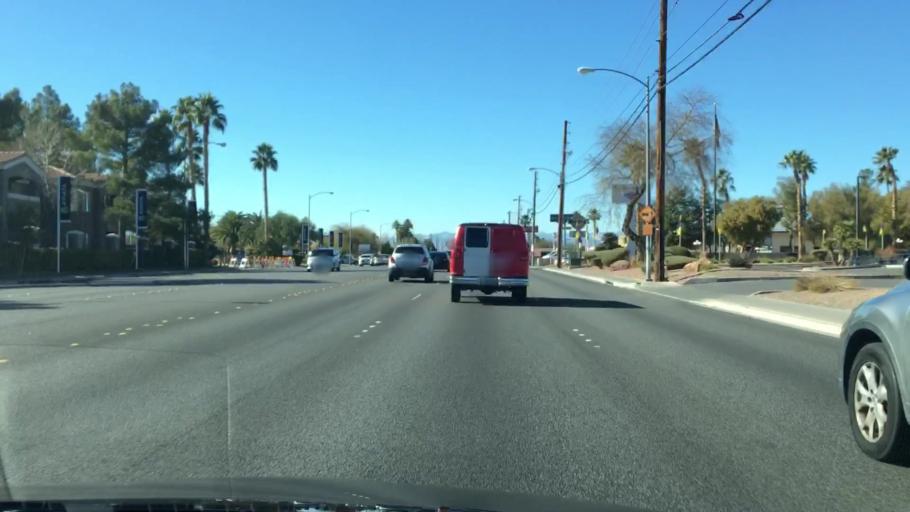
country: US
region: Nevada
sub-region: Clark County
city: Whitney
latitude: 36.0572
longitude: -115.1211
